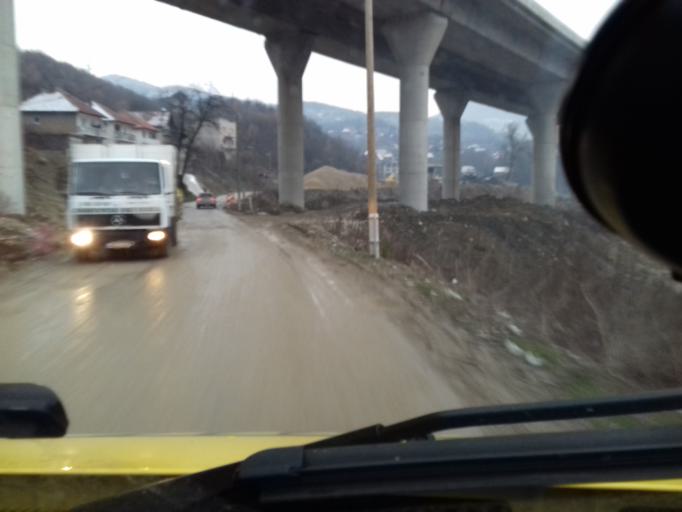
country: BA
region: Federation of Bosnia and Herzegovina
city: Zenica
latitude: 44.1811
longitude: 17.9727
